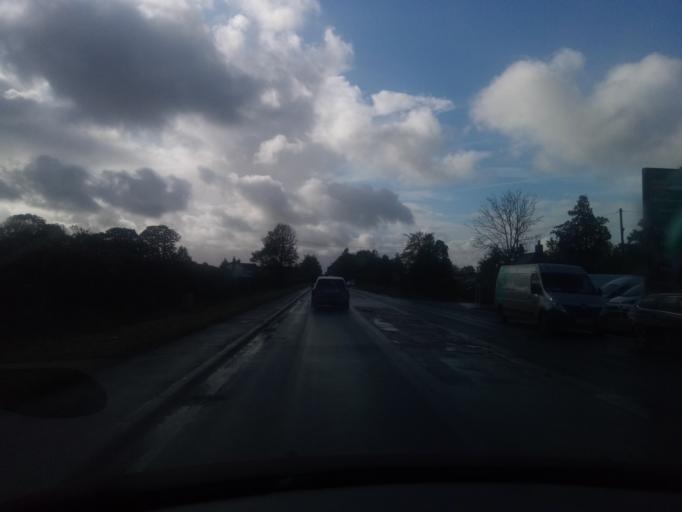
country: GB
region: England
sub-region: Cumbria
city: Carlisle
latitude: 54.9407
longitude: -2.9442
